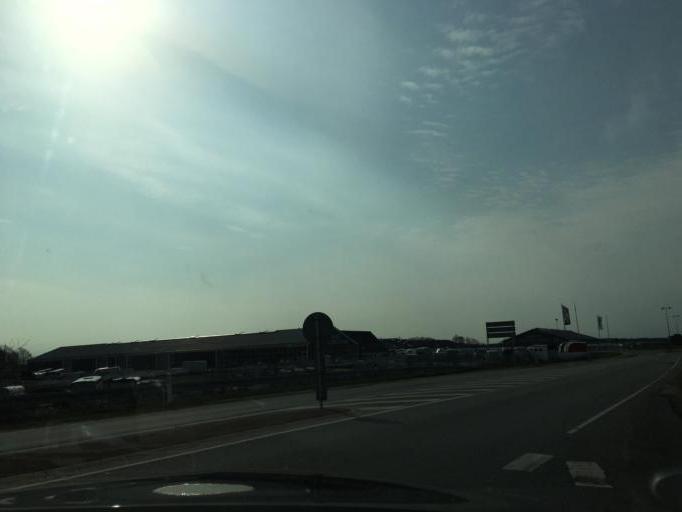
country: DK
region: South Denmark
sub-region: Vejen Kommune
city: Brorup
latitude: 55.5036
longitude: 9.0211
